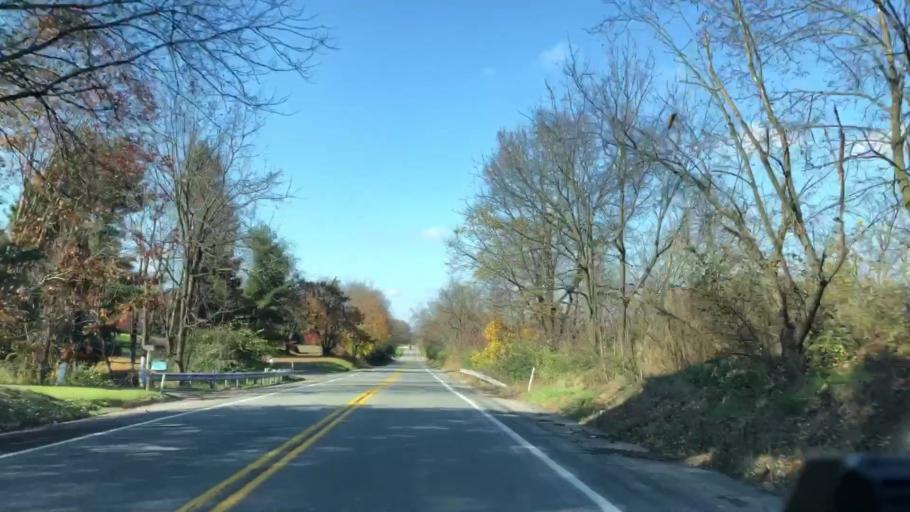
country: US
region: Pennsylvania
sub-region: Montgomery County
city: Sanatoga
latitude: 40.2147
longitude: -75.6026
